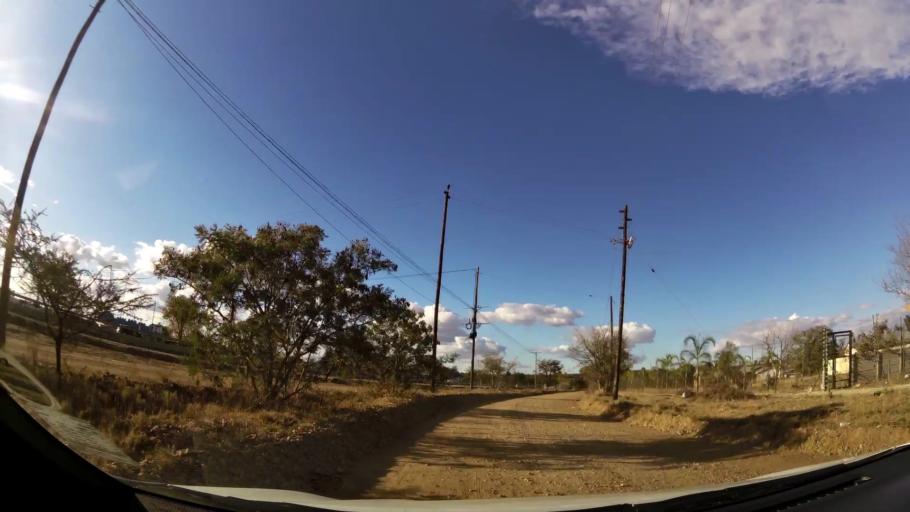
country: ZA
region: Limpopo
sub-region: Capricorn District Municipality
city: Polokwane
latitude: -23.9330
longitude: 29.4235
